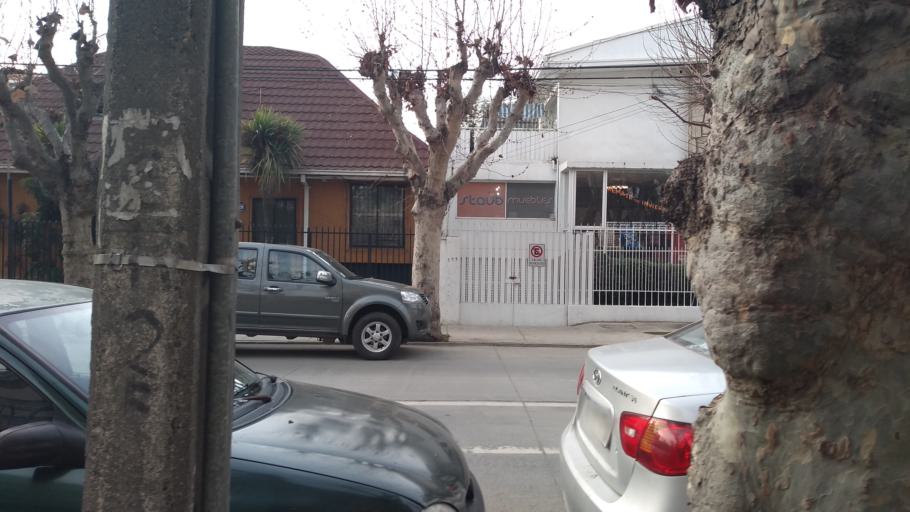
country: CL
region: Valparaiso
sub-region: Provincia de Valparaiso
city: Vina del Mar
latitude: -33.0210
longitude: -71.5553
